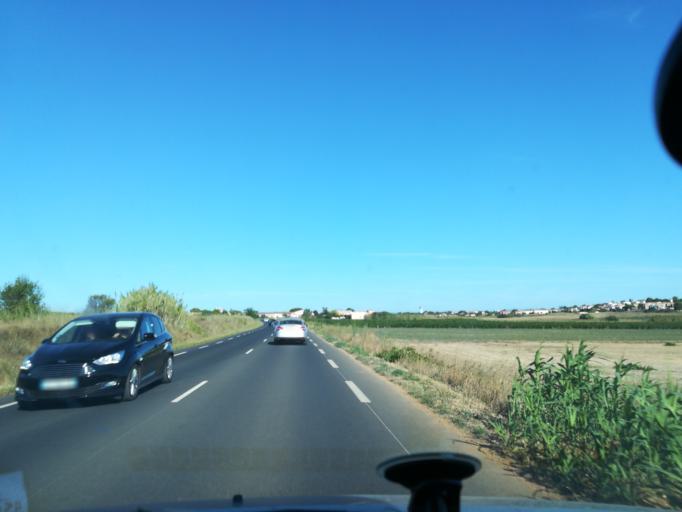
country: FR
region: Languedoc-Roussillon
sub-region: Departement de l'Herault
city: Portiragnes
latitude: 43.2963
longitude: 3.3515
